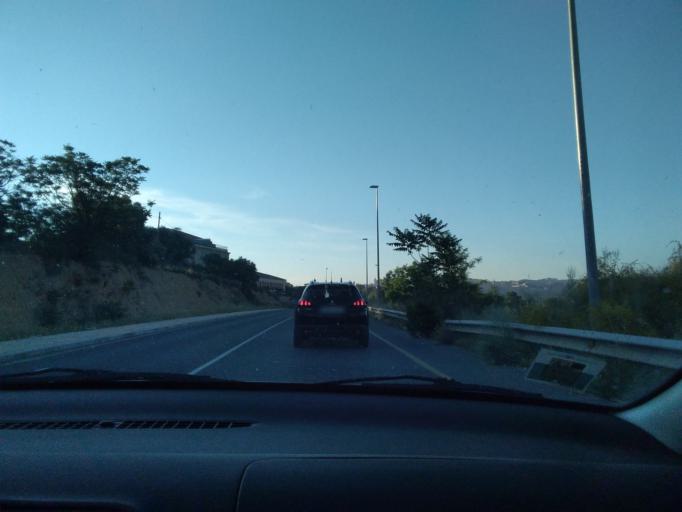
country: ES
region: Castille-La Mancha
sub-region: Province of Toledo
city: Toledo
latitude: 39.8777
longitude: -4.0455
